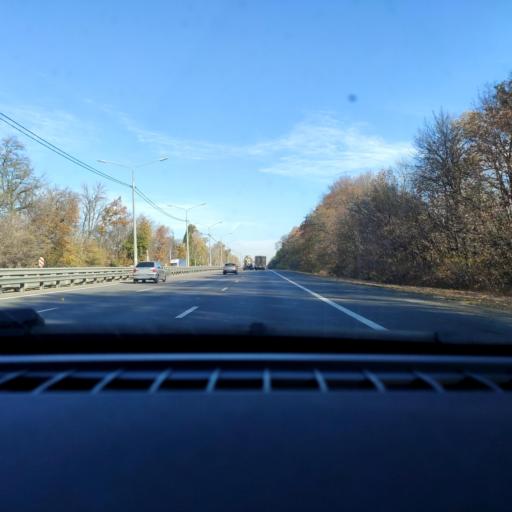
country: RU
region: Voronezj
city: Podgornoye
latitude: 51.8145
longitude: 39.2075
